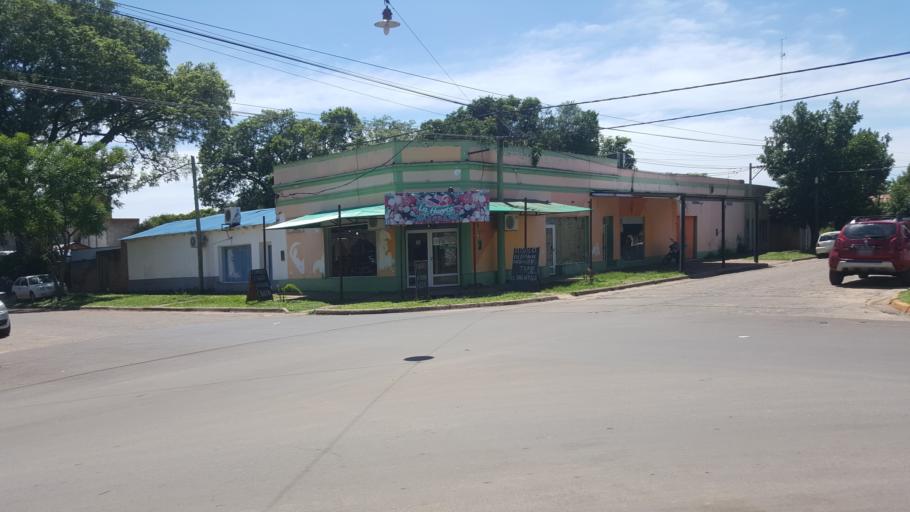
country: AR
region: Corrientes
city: Ituzaingo
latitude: -27.5884
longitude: -56.6886
